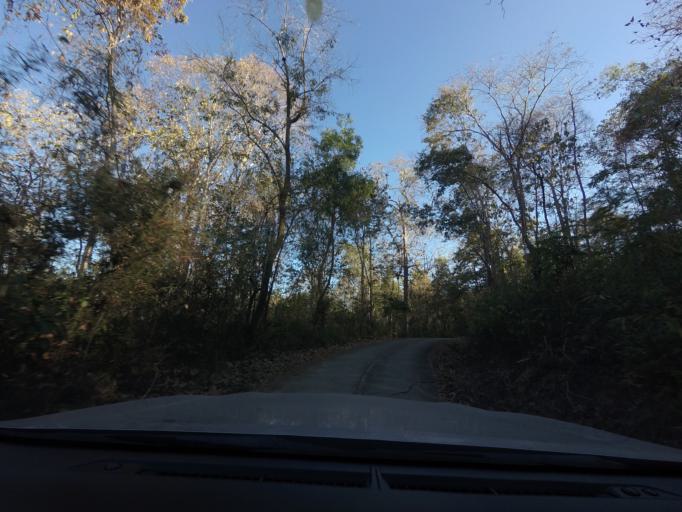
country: TH
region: Mae Hong Son
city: Wiang Nuea
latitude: 19.4017
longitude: 98.4182
